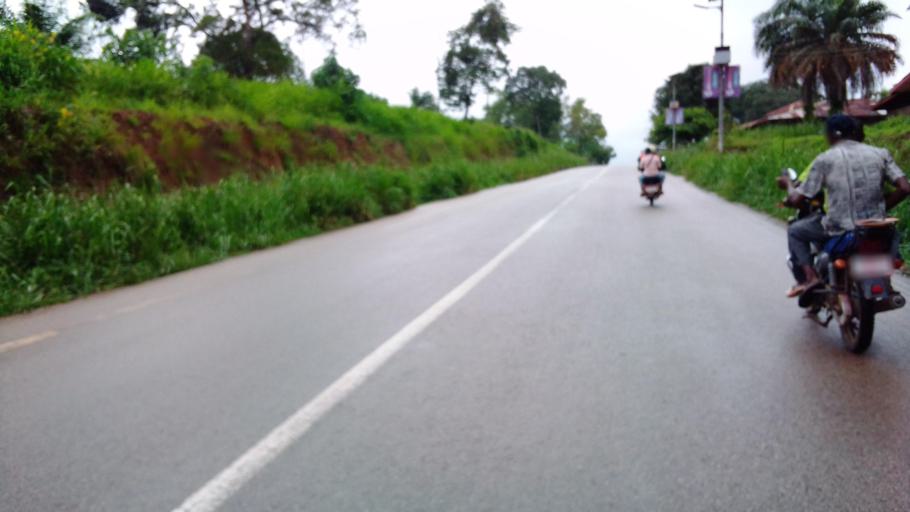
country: SL
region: Eastern Province
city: Kenema
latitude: 7.8764
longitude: -11.1759
